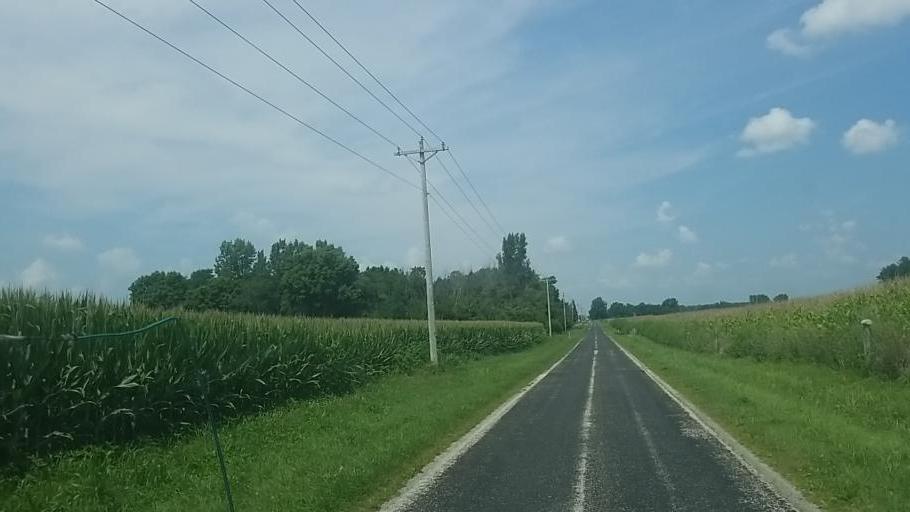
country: US
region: Ohio
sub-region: Union County
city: Richwood
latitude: 40.6245
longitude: -83.3617
